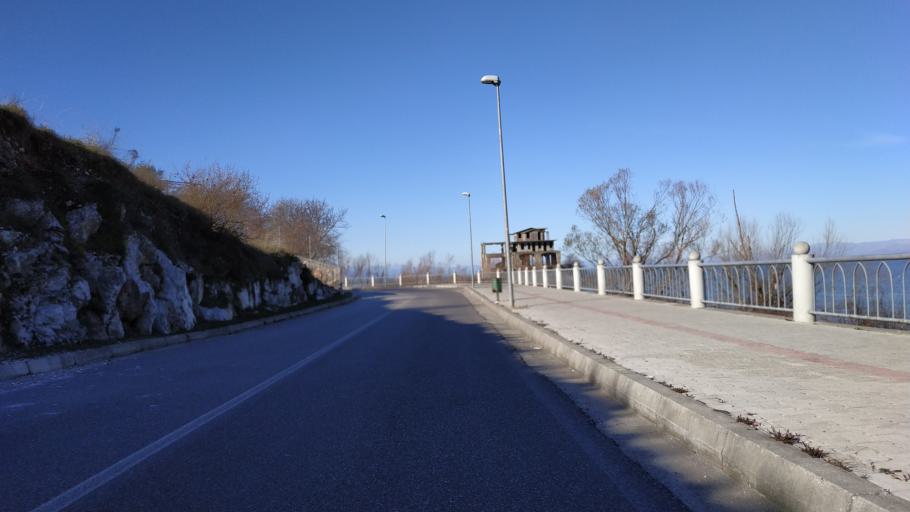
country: AL
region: Shkoder
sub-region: Rrethi i Shkodres
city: Berdica e Madhe
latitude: 42.0581
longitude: 19.4633
